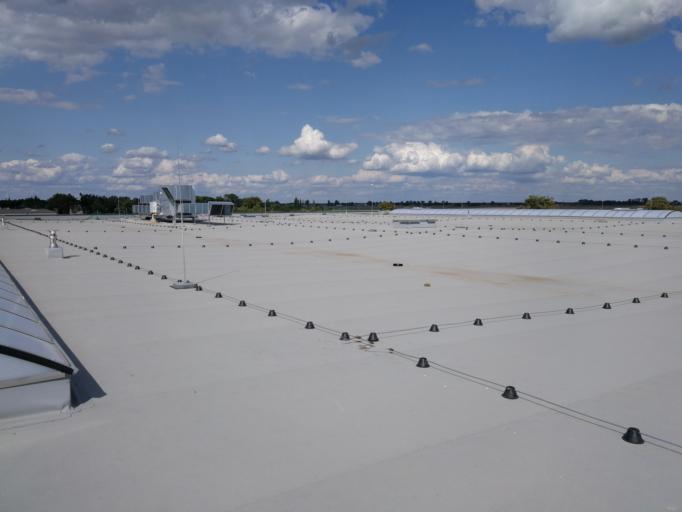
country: PL
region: Kujawsko-Pomorskie
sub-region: Powiat torunski
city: Lysomice
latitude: 53.1018
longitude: 18.6256
